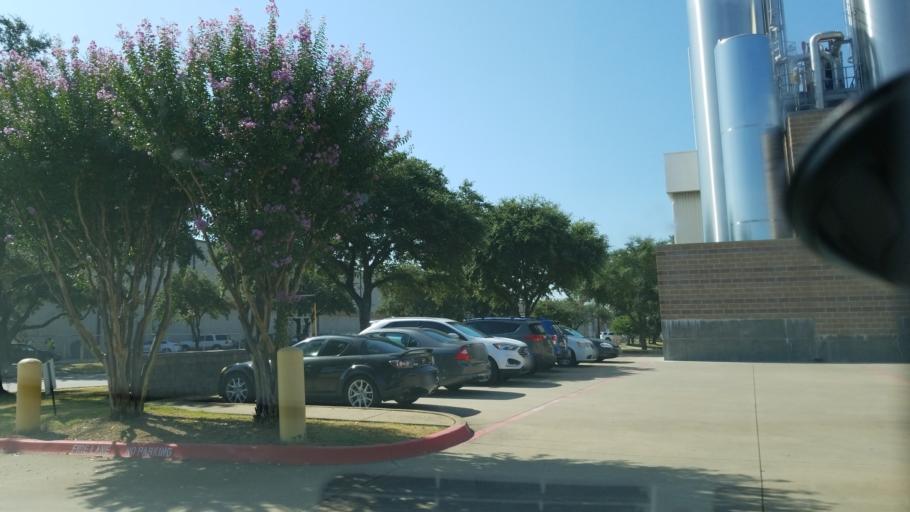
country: US
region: Texas
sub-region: Dallas County
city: Cockrell Hill
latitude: 32.7053
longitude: -96.9184
